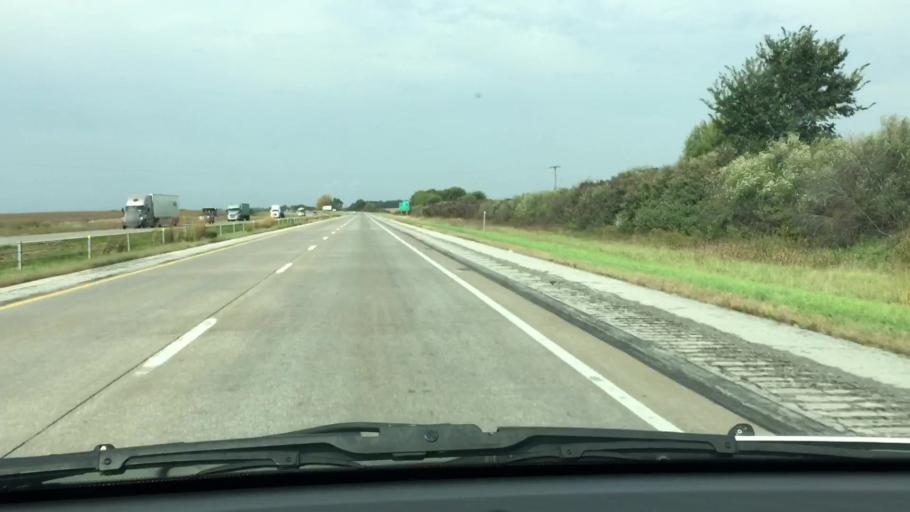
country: US
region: Iowa
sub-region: Scott County
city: Walcott
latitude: 41.6306
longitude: -90.8300
